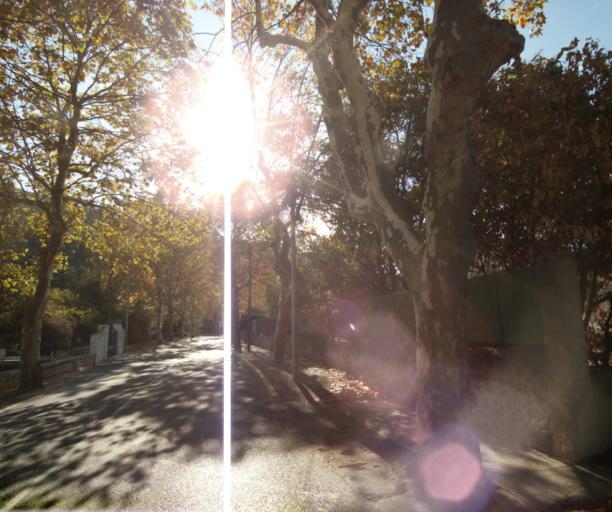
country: FR
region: Provence-Alpes-Cote d'Azur
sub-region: Departement des Bouches-du-Rhone
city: Allauch
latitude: 43.3611
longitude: 5.4939
